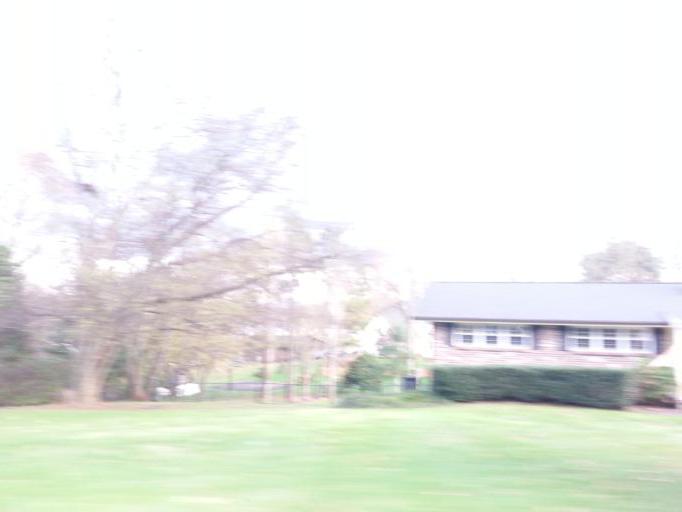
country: US
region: Tennessee
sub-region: Knox County
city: Knoxville
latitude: 35.9286
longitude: -84.0160
